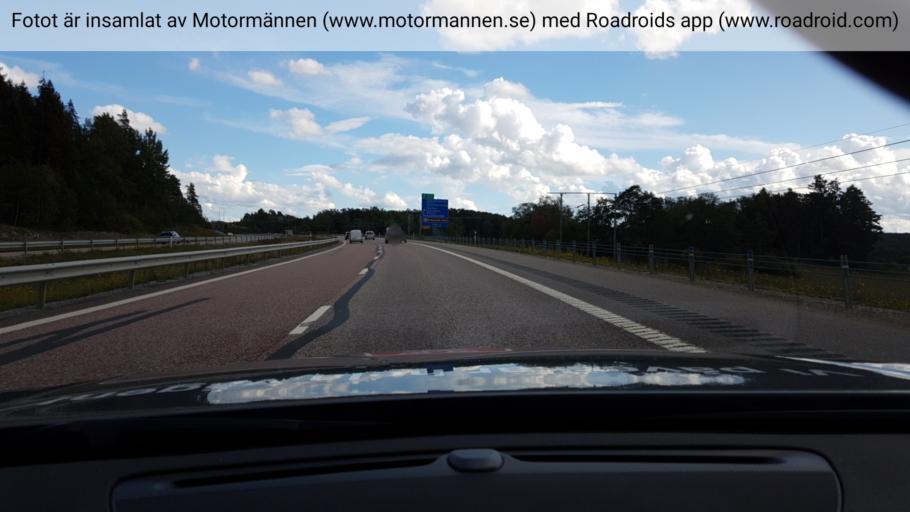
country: SE
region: Soedermanland
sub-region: Strangnas Kommun
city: Mariefred
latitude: 59.2541
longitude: 17.1512
